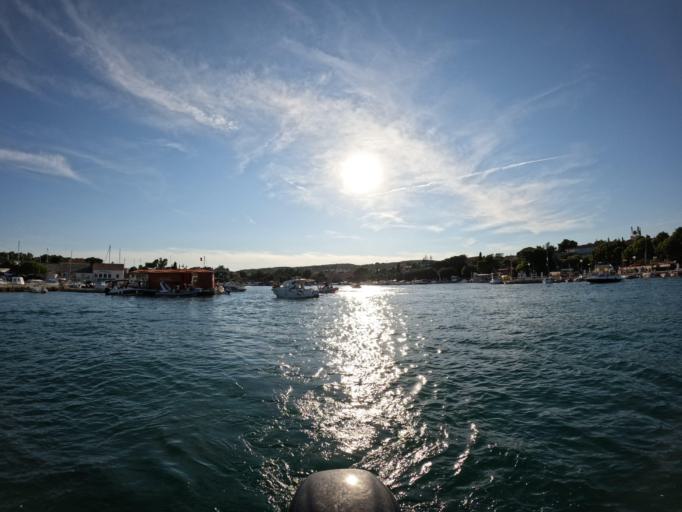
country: HR
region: Primorsko-Goranska
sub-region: Grad Krk
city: Krk
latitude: 45.0247
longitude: 14.5743
